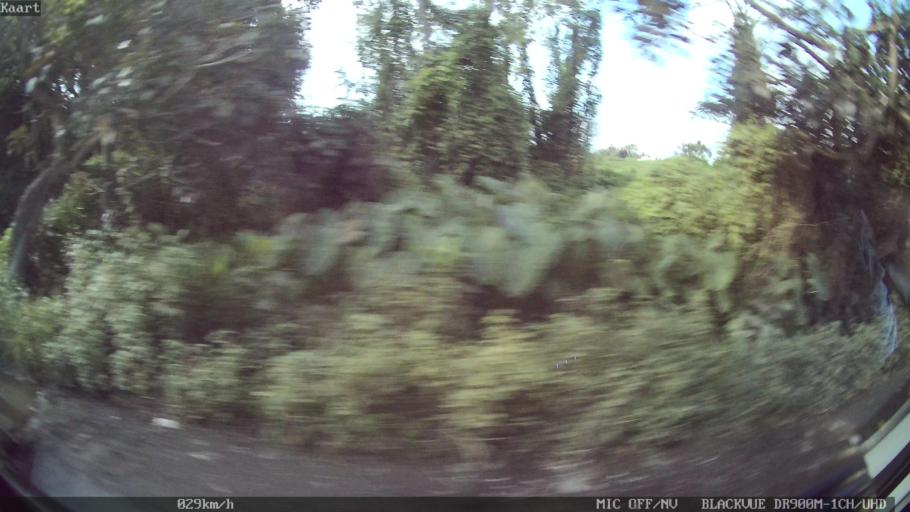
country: ID
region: Bali
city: Banjar Pekenjelodan
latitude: -8.5724
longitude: 115.1900
